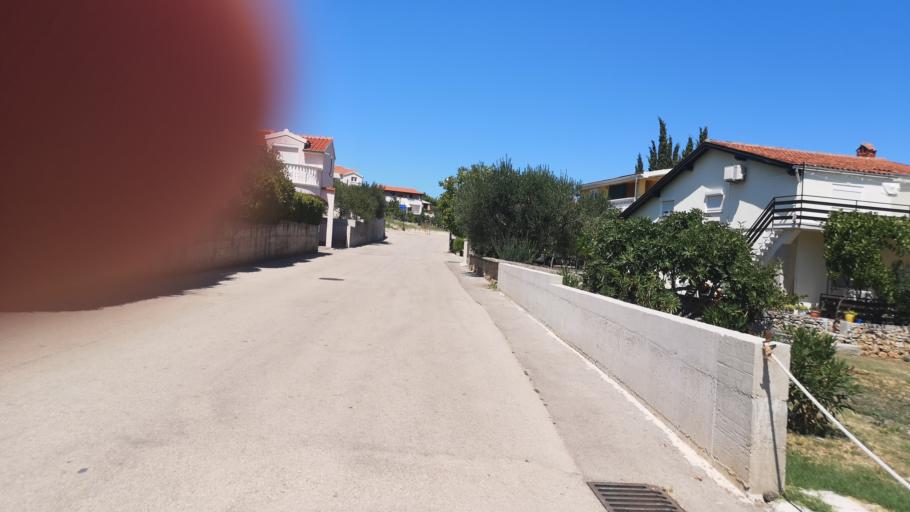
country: HR
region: Sibensko-Kniniska
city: Vodice
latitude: 43.7612
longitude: 15.7690
